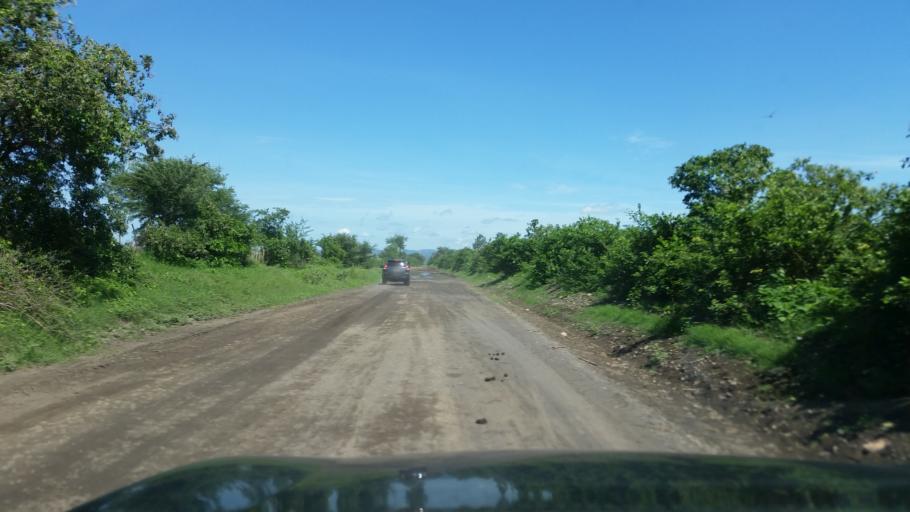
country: NI
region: Chinandega
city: Puerto Morazan
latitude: 12.7719
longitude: -87.0918
